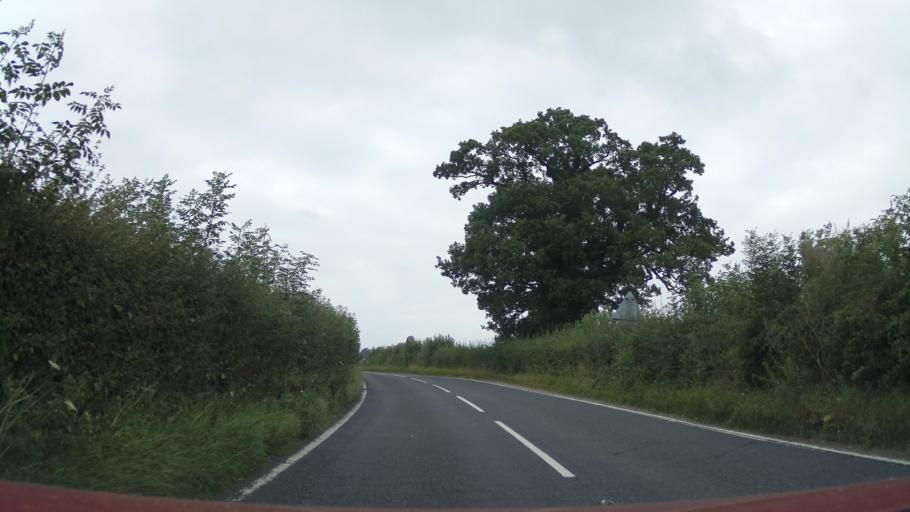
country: GB
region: England
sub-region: Derbyshire
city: Belper
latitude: 53.0200
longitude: -1.5454
